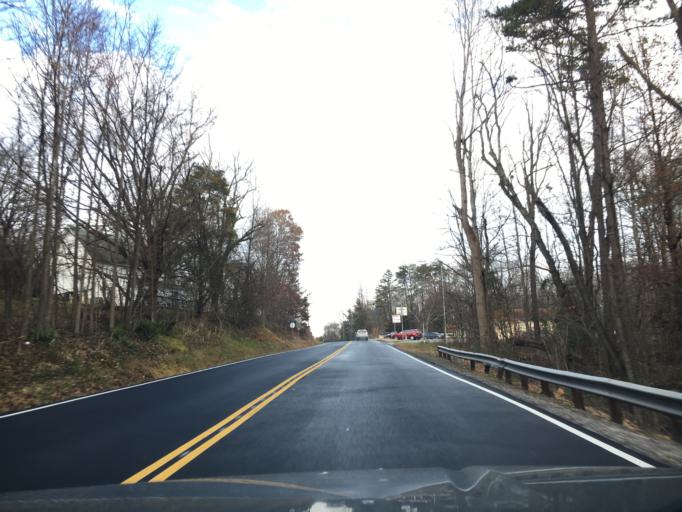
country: US
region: Virginia
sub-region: Prince Edward County
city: Farmville
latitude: 37.3164
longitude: -78.3859
